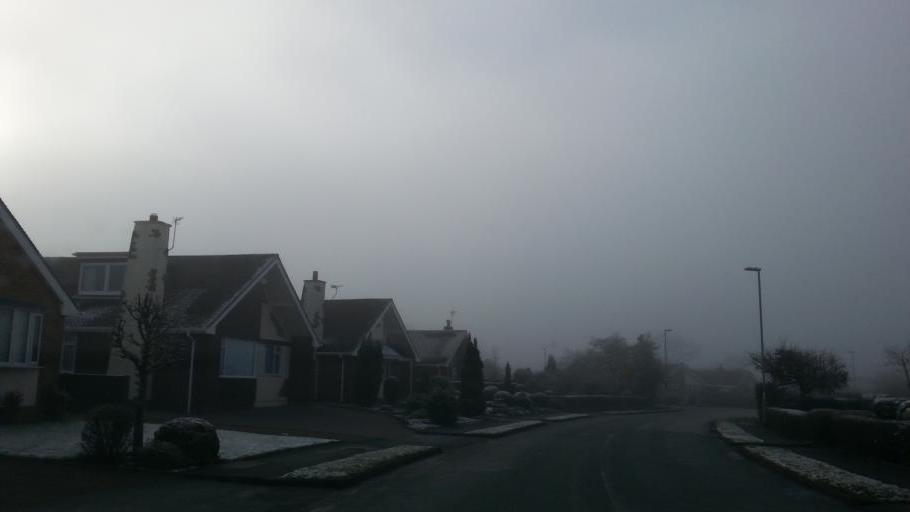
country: GB
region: England
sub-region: Staffordshire
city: Biddulph
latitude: 53.1220
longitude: -2.1580
